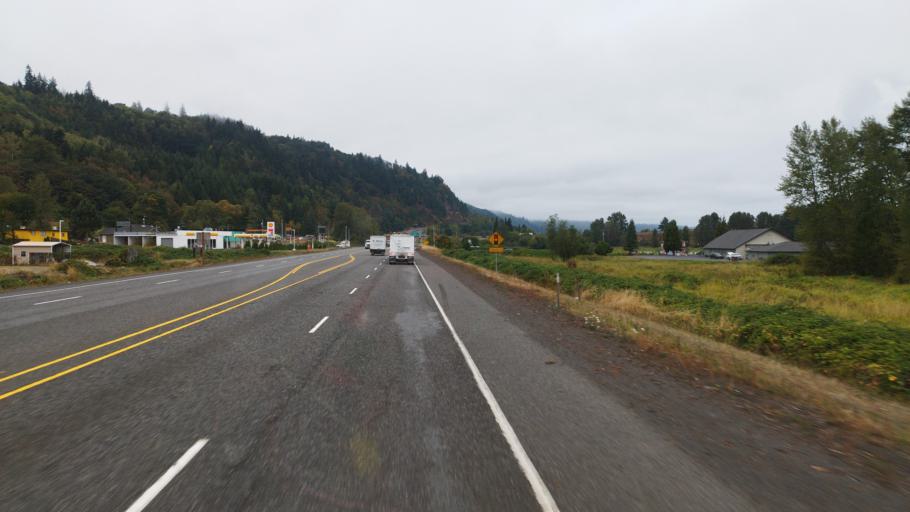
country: US
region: Oregon
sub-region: Columbia County
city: Rainier
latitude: 46.0947
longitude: -122.9599
